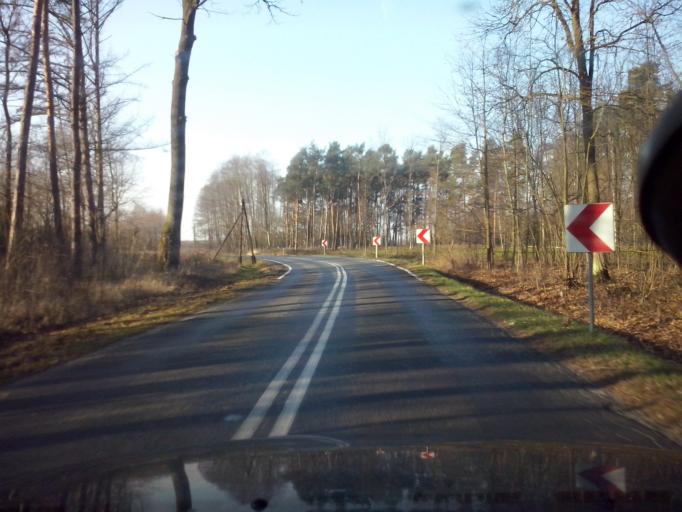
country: PL
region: Subcarpathian Voivodeship
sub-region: Powiat lezajski
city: Letownia
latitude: 50.3645
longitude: 22.2421
